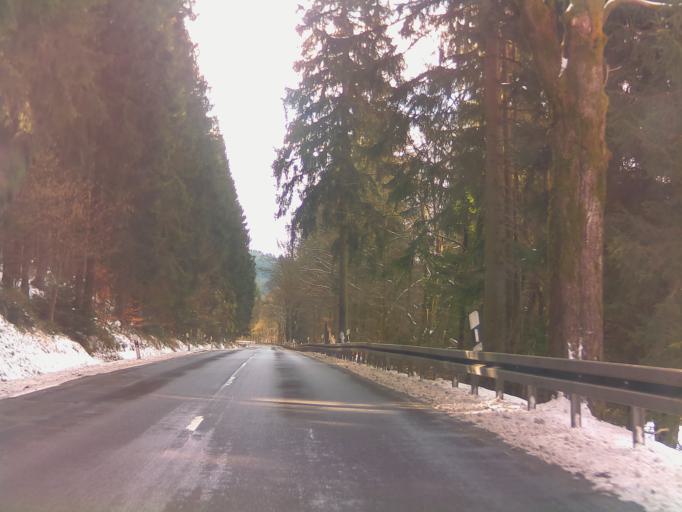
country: DE
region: Thuringia
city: Schwarza
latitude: 50.6236
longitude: 10.5529
